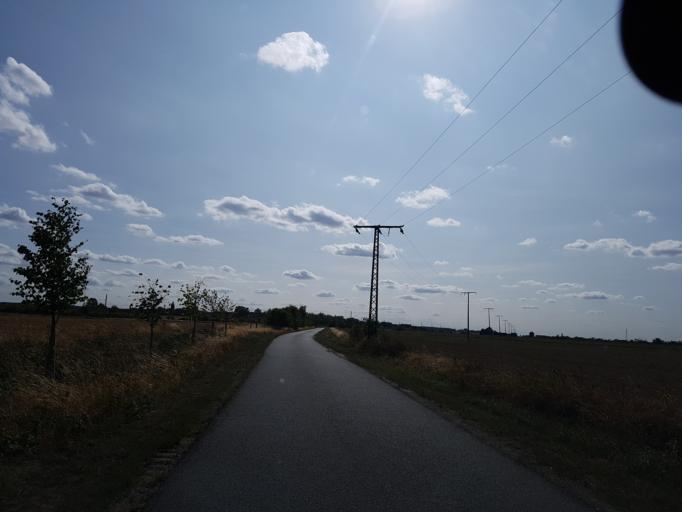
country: DE
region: Saxony-Anhalt
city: Seyda
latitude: 51.9536
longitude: 12.8756
